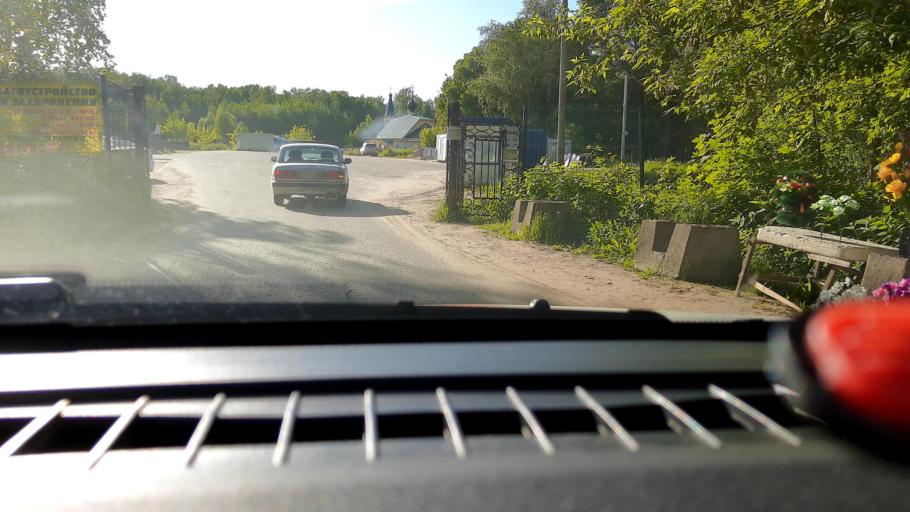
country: RU
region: Nizjnij Novgorod
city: Gorbatovka
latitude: 56.2312
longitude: 43.7628
